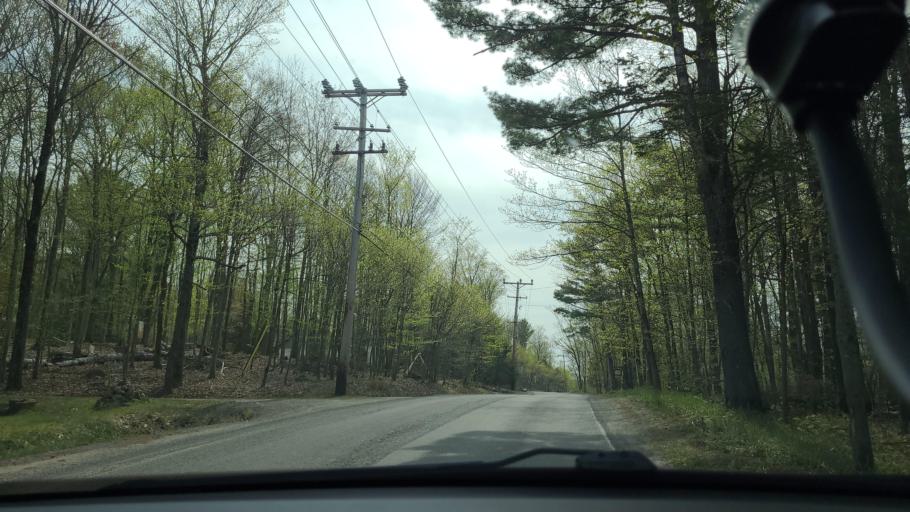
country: CA
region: Quebec
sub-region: Laurentides
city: Prevost
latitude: 45.8920
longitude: -74.0452
